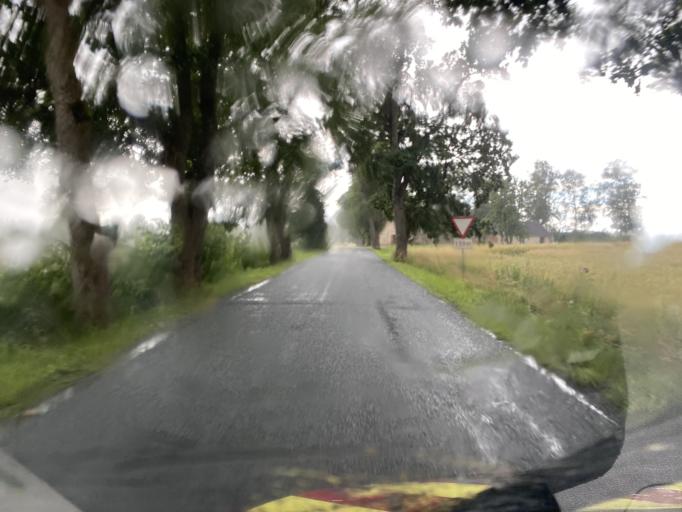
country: EE
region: Valgamaa
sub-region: Torva linn
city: Torva
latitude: 58.1392
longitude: 25.8051
